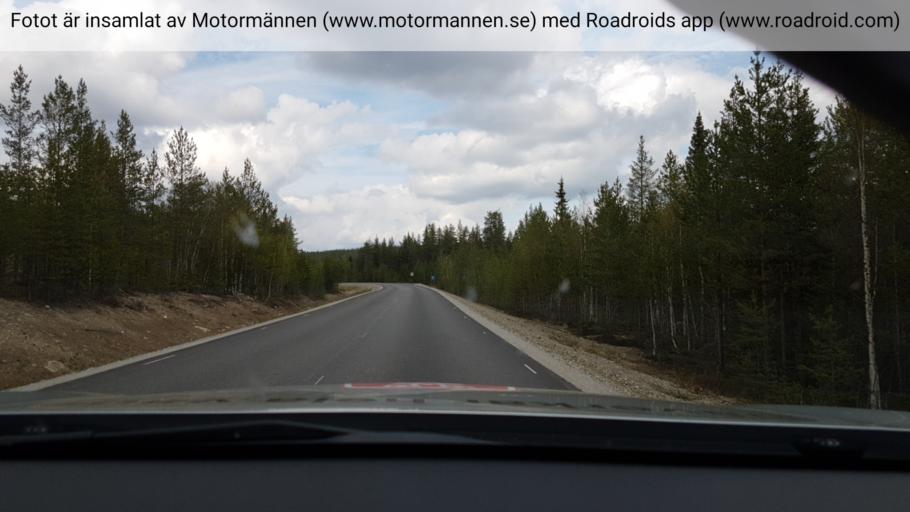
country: SE
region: Vaesterbotten
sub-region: Lycksele Kommun
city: Lycksele
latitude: 64.0134
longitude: 18.4576
